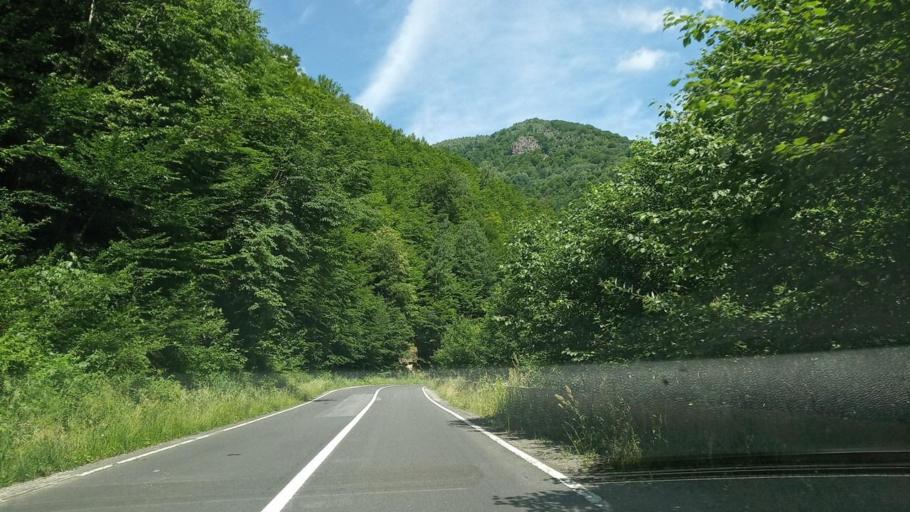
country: RO
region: Alba
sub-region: Comuna Sugag
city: Sugag
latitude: 45.7190
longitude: 23.6033
